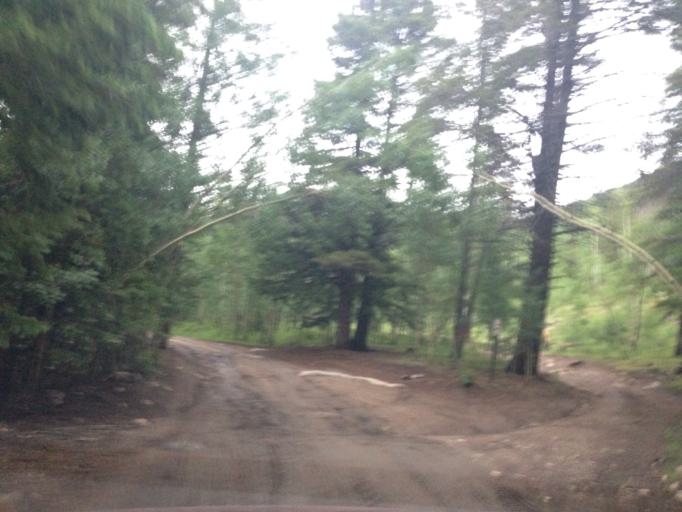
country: US
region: Colorado
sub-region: Clear Creek County
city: Georgetown
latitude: 39.5522
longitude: -105.7531
